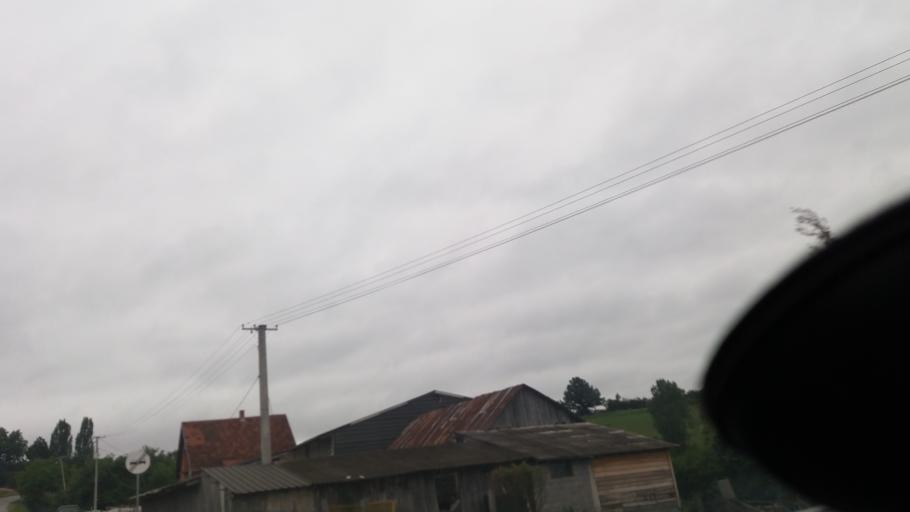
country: RS
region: Central Serbia
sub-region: Kolubarski Okrug
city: Ljig
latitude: 44.2429
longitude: 20.2123
